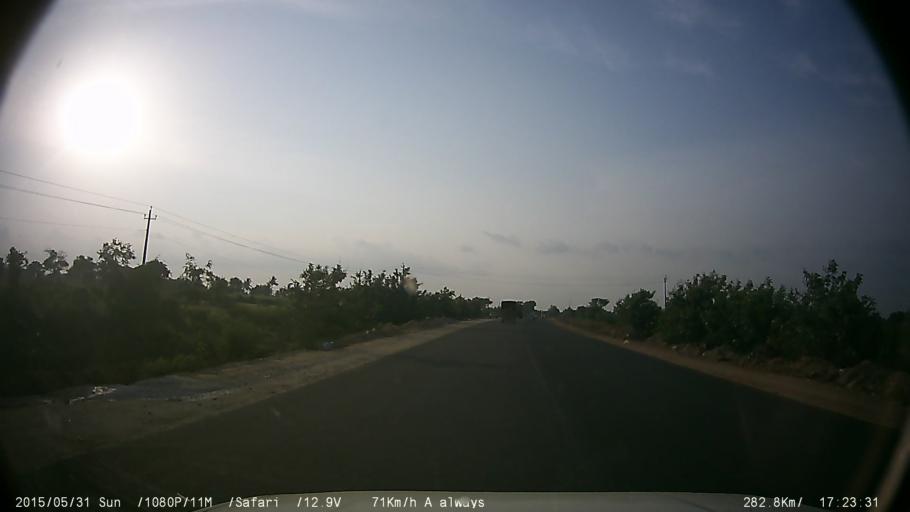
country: IN
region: Karnataka
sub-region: Chamrajnagar
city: Gundlupet
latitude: 11.8406
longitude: 76.6740
